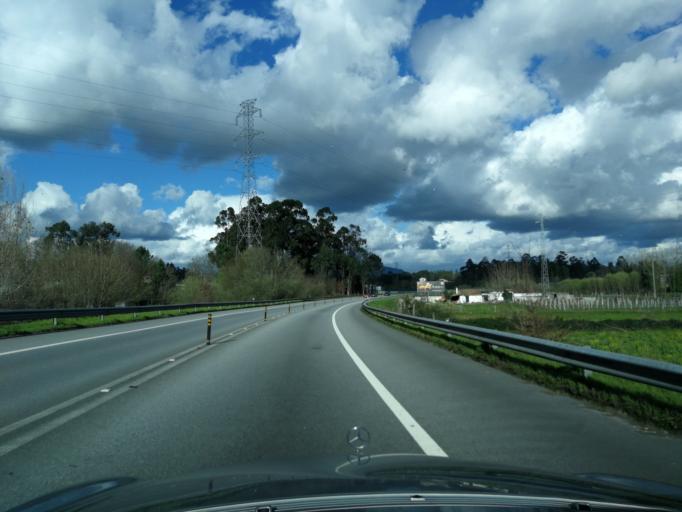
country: PT
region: Braga
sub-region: Vila Verde
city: Prado
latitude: 41.6159
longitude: -8.4506
